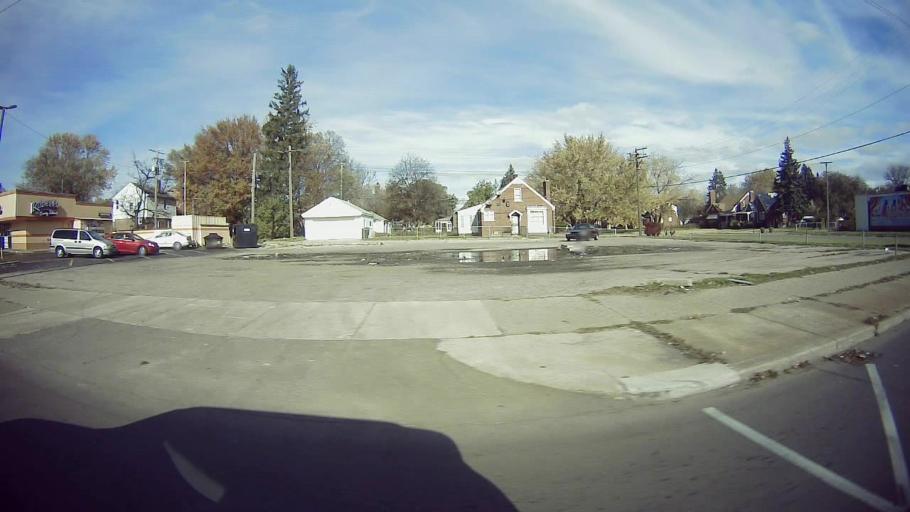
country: US
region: Michigan
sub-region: Macomb County
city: Eastpointe
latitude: 42.4347
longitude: -82.9941
